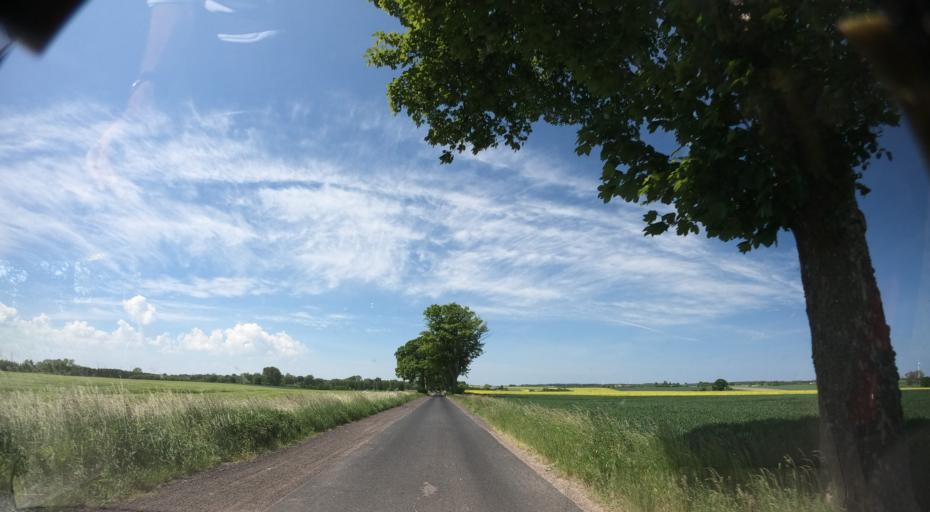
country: PL
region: West Pomeranian Voivodeship
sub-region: Powiat kolobrzeski
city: Dygowo
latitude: 54.1434
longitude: 15.7437
